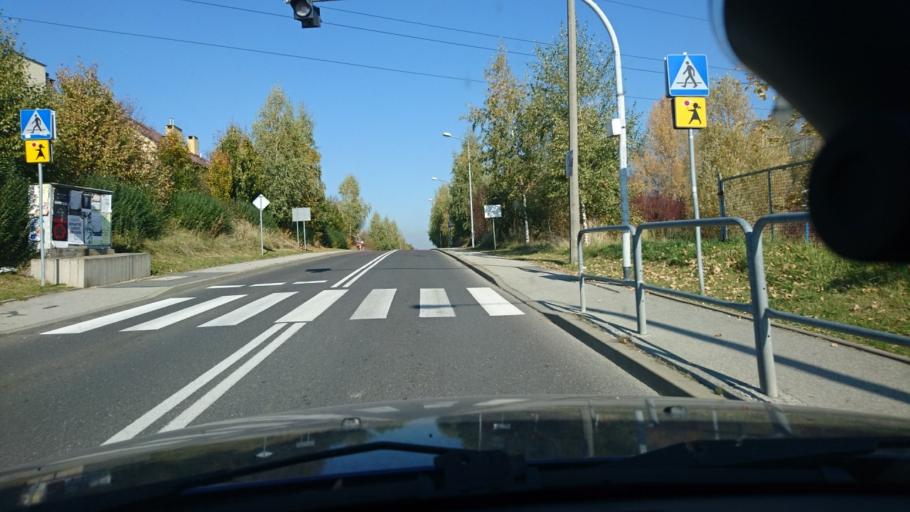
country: PL
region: Silesian Voivodeship
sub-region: Bielsko-Biala
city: Bielsko-Biala
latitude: 49.8333
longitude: 19.0294
